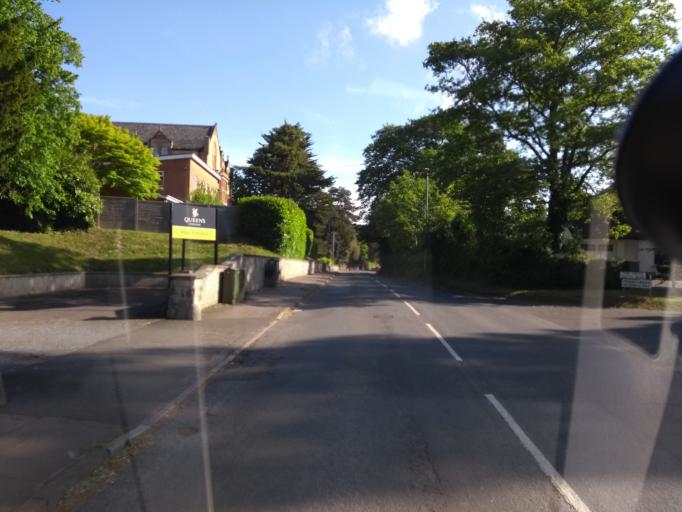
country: GB
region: England
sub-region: Somerset
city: Taunton
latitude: 51.0025
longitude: -3.1150
